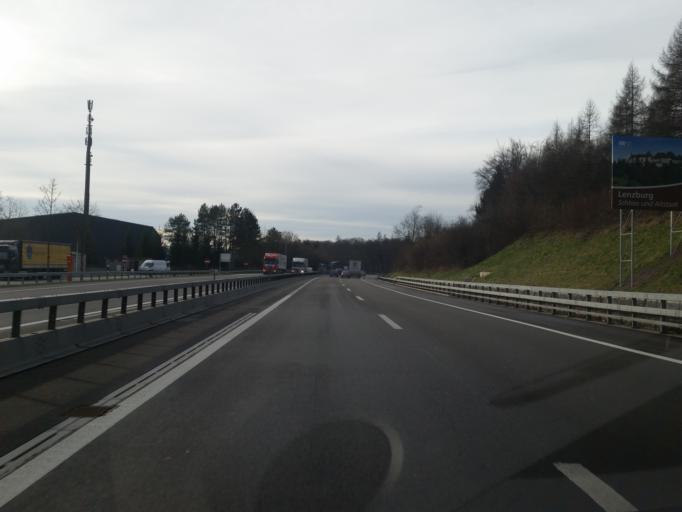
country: CH
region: Aargau
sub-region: Bezirk Lenzburg
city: Othmarsingen
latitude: 47.4031
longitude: 8.2075
